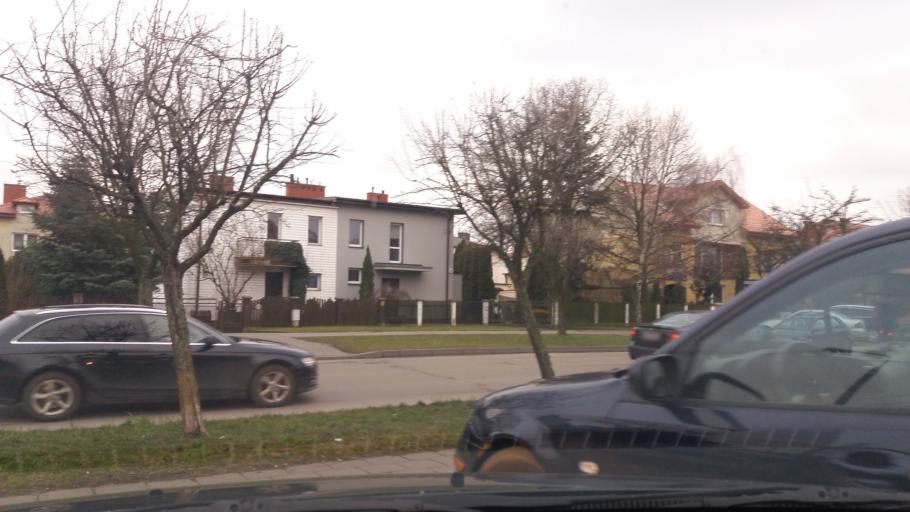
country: PL
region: Masovian Voivodeship
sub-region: Powiat mlawski
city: Mlawa
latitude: 53.1075
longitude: 20.3788
